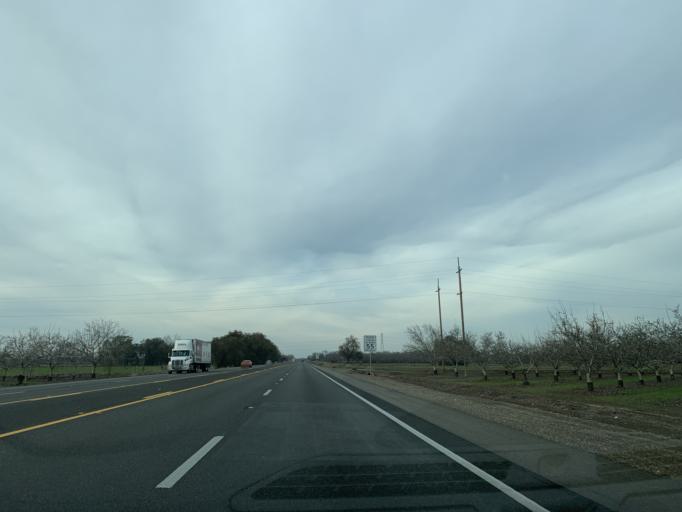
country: US
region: California
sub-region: Yuba County
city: Plumas Lake
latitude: 38.8886
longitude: -121.5734
